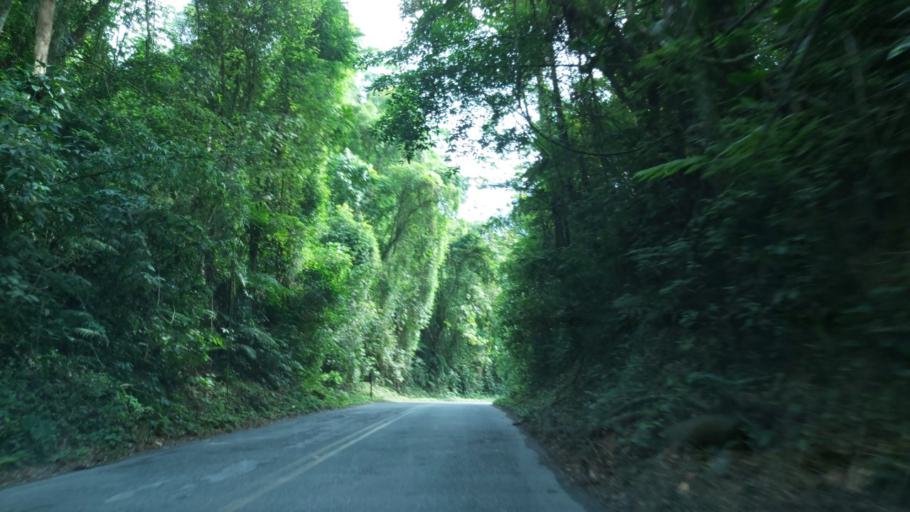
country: BR
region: Sao Paulo
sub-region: Juquia
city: Juquia
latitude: -24.0849
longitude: -47.6098
